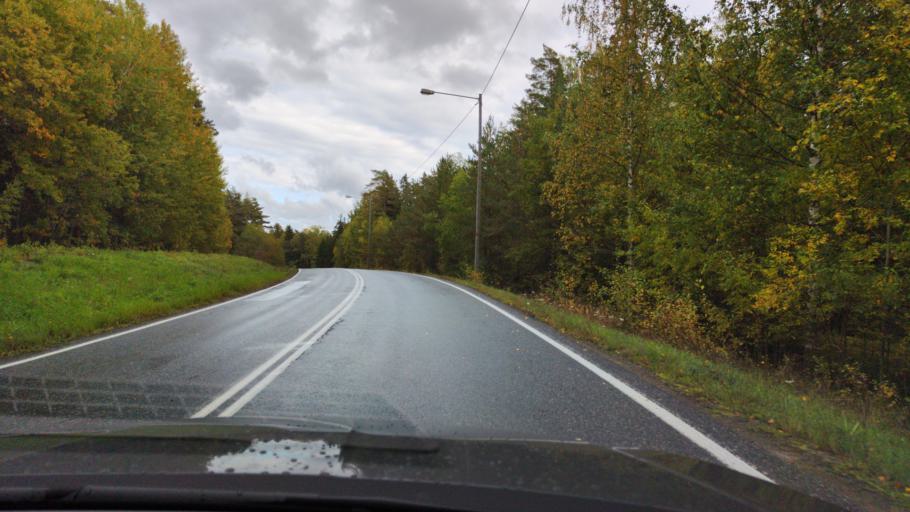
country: FI
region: Varsinais-Suomi
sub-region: Aboland-Turunmaa
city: Pargas
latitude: 60.3700
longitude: 22.2567
